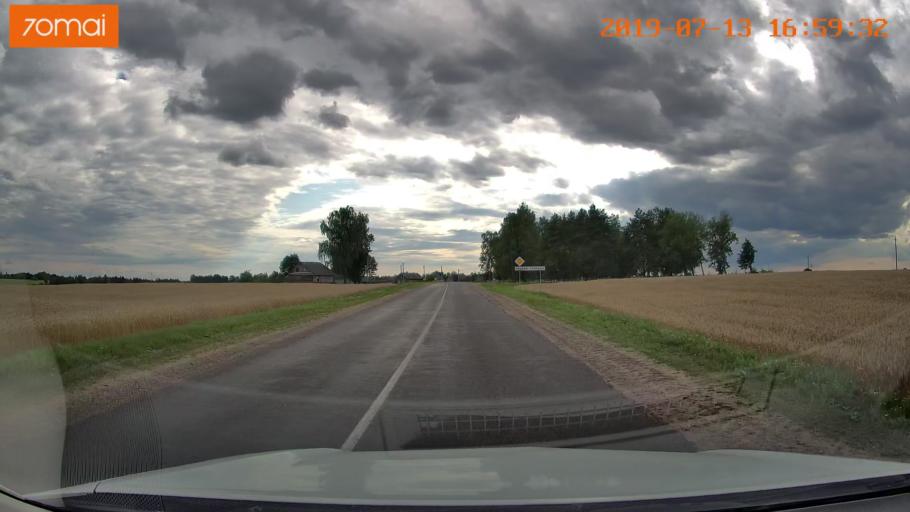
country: BY
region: Mogilev
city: Kirawsk
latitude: 53.2973
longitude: 29.4273
